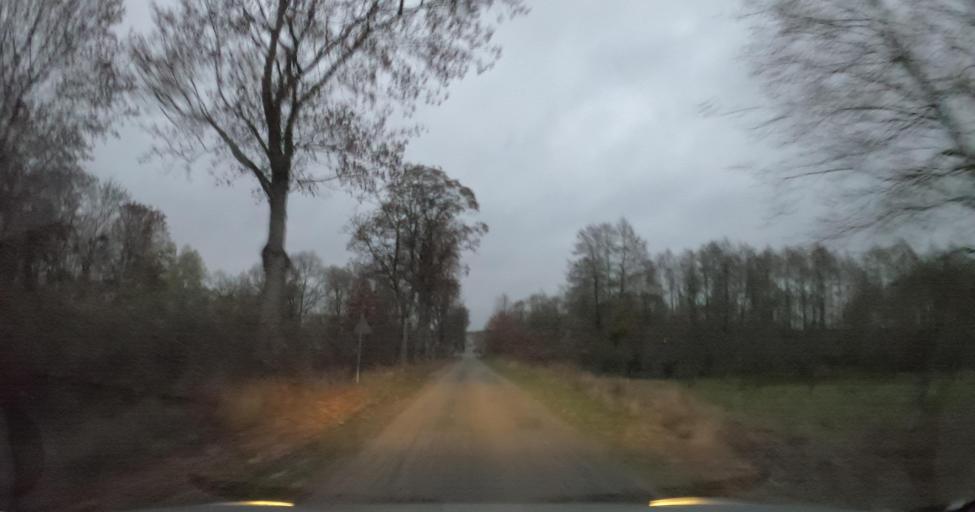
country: PL
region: West Pomeranian Voivodeship
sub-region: Powiat bialogardzki
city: Tychowo
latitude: 53.8537
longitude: 16.2411
